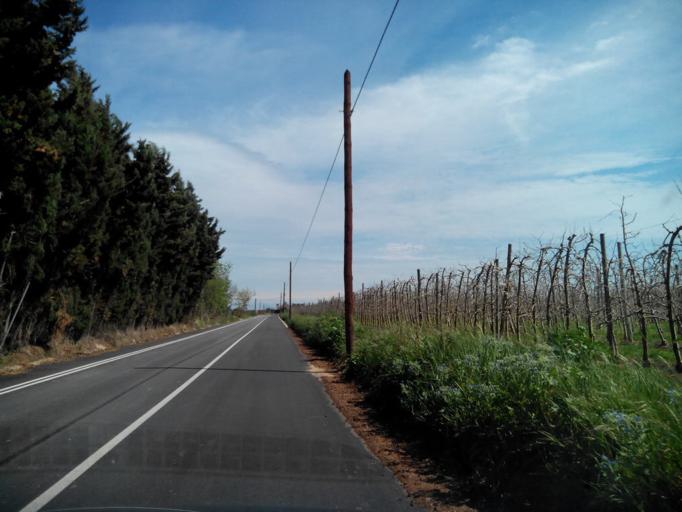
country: ES
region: Catalonia
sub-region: Provincia de Girona
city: Sant Pere Pescador
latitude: 42.1876
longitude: 3.0935
